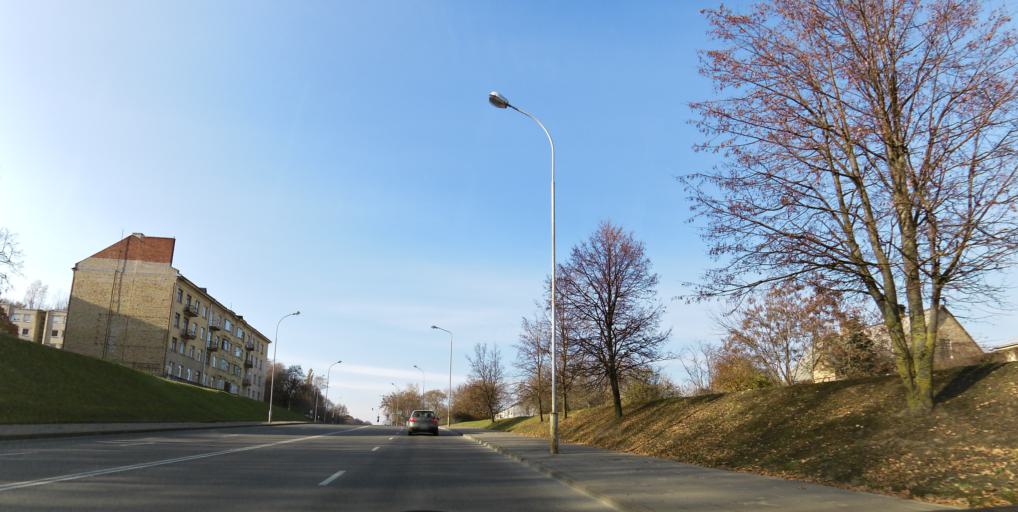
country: LT
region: Vilnius County
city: Rasos
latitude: 54.6770
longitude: 25.3058
